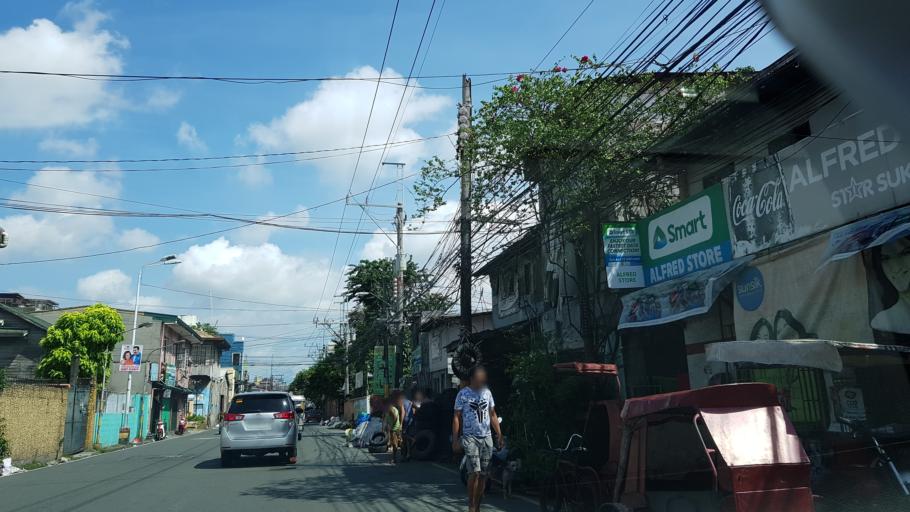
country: PH
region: Metro Manila
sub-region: Mandaluyong
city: Mandaluyong City
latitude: 14.5781
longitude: 121.0097
